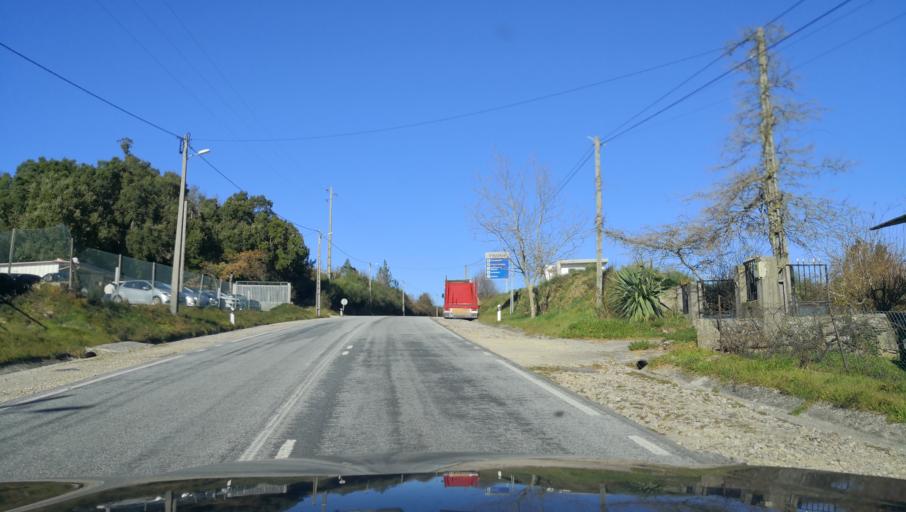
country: PT
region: Viseu
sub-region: Vouzela
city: Vouzela
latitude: 40.6893
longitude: -8.1433
